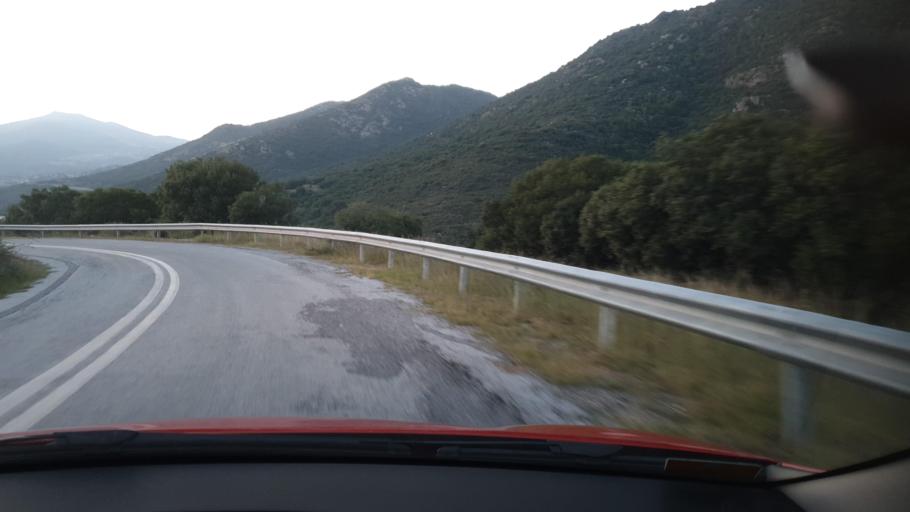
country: GR
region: Central Macedonia
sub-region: Nomos Thessalonikis
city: Peristera
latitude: 40.5239
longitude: 23.2019
